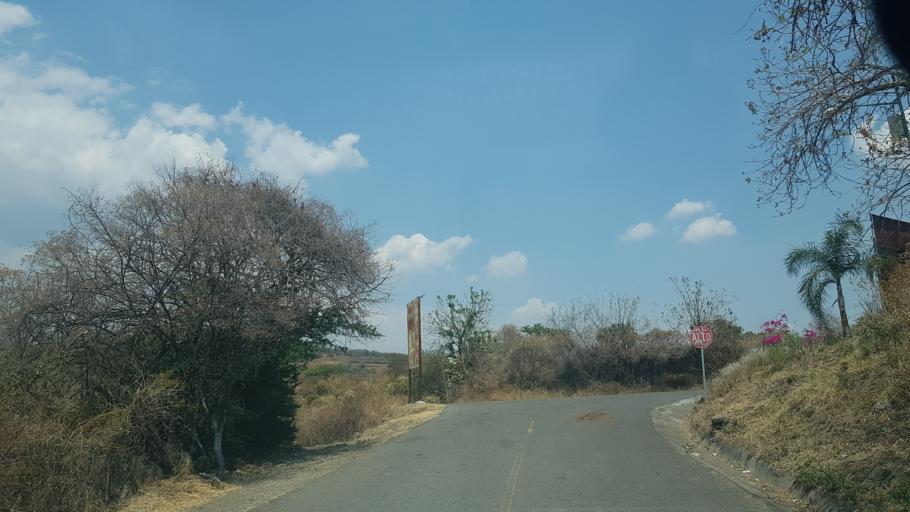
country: MX
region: Puebla
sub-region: Atzitzihuacan
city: Santiago Atzitzihuacan
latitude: 18.8364
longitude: -98.5770
